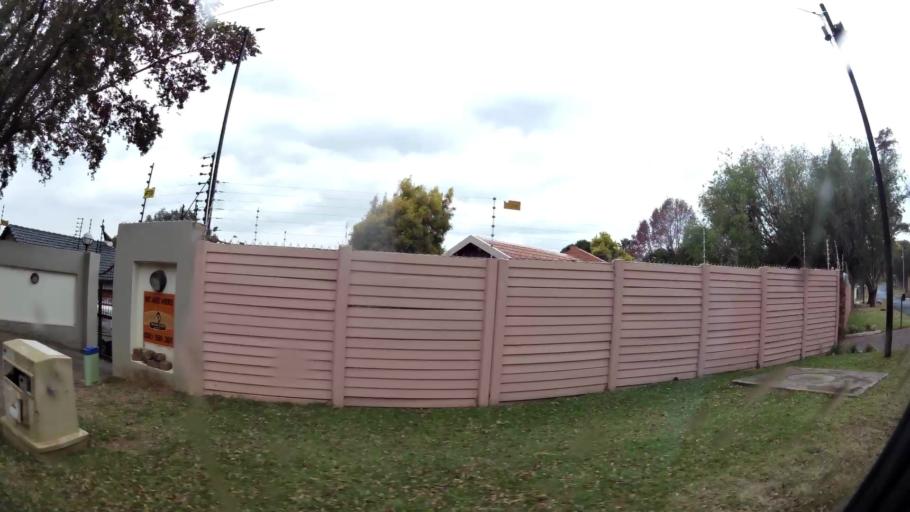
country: ZA
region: Gauteng
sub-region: City of Johannesburg Metropolitan Municipality
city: Roodepoort
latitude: -26.1030
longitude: 27.9196
